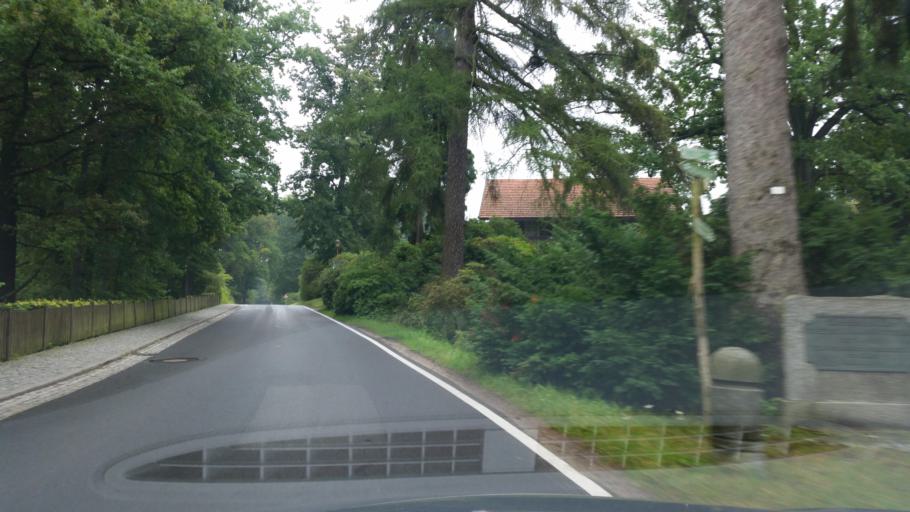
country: DE
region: Saxony
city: Weisswasser
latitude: 51.5372
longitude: 14.6318
